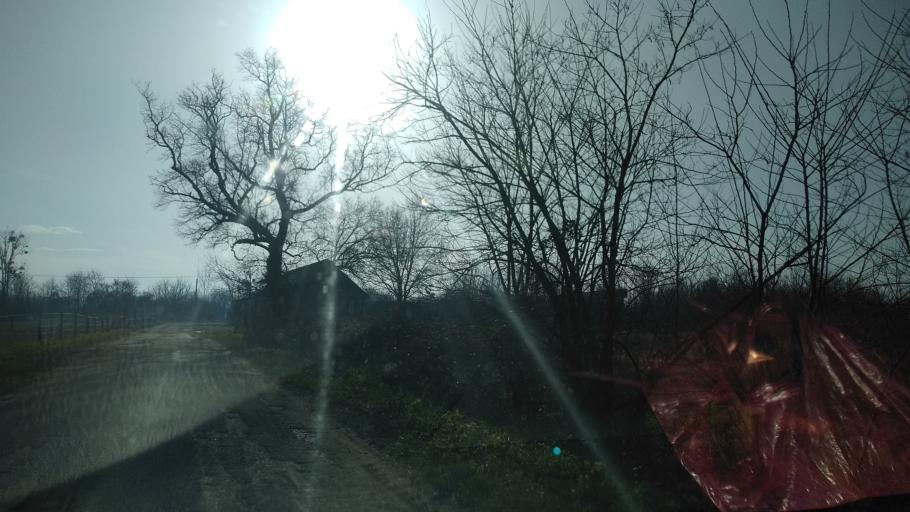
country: HU
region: Somogy
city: Barcs
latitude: 45.9573
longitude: 17.4877
